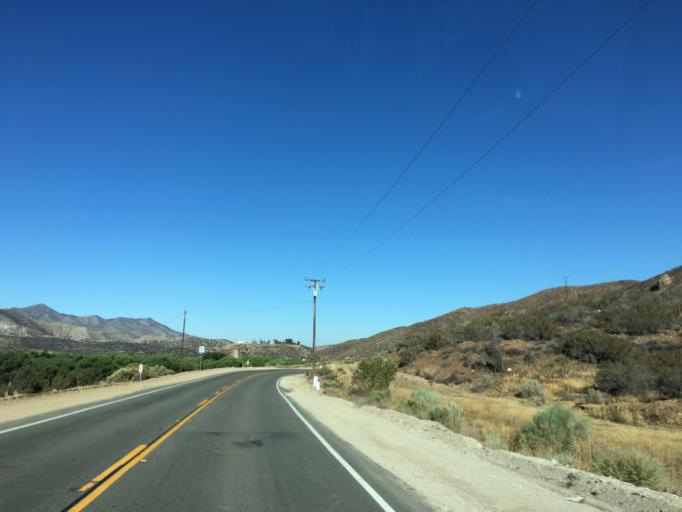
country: US
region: California
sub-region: Los Angeles County
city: Acton
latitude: 34.4377
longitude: -118.2356
